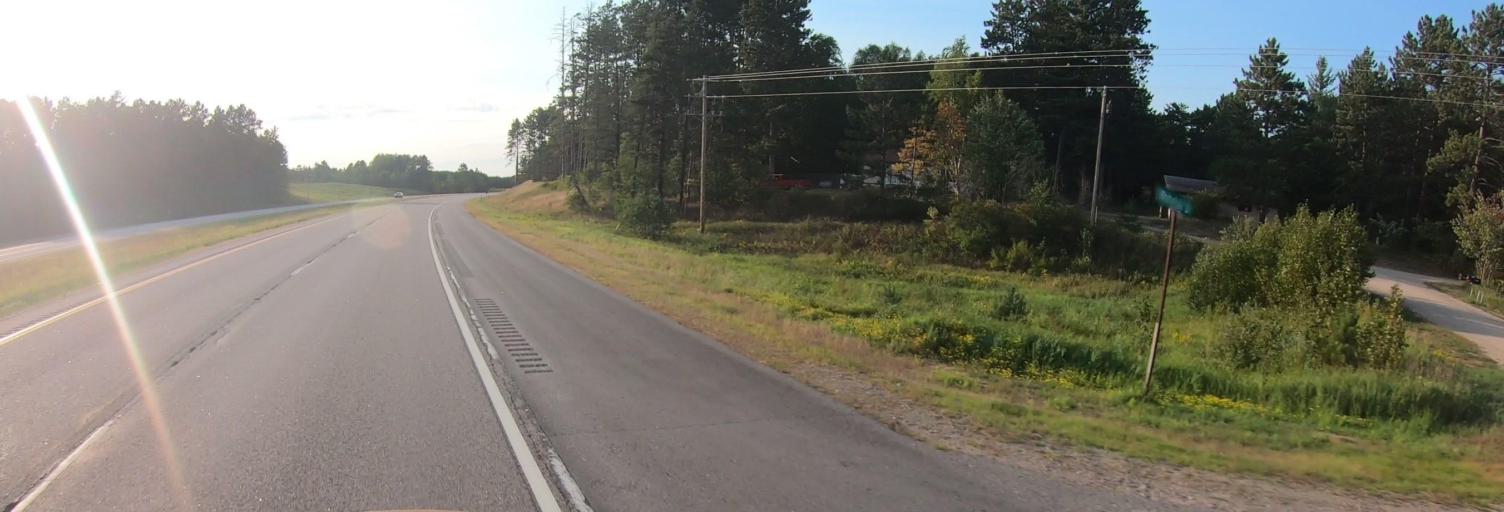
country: US
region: Minnesota
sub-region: Saint Louis County
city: Mountain Iron
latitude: 47.6710
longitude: -92.6316
